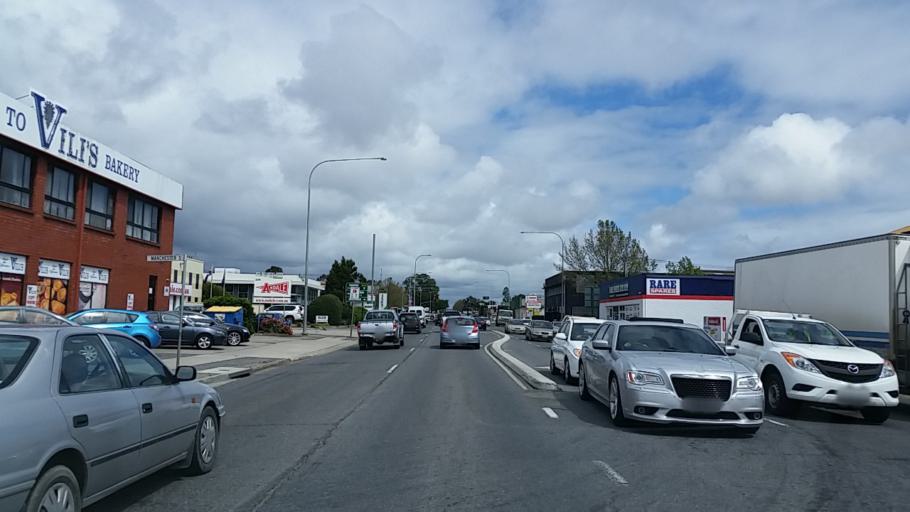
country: AU
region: South Australia
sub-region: Unley
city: Forestville
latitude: -34.9392
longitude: 138.5709
